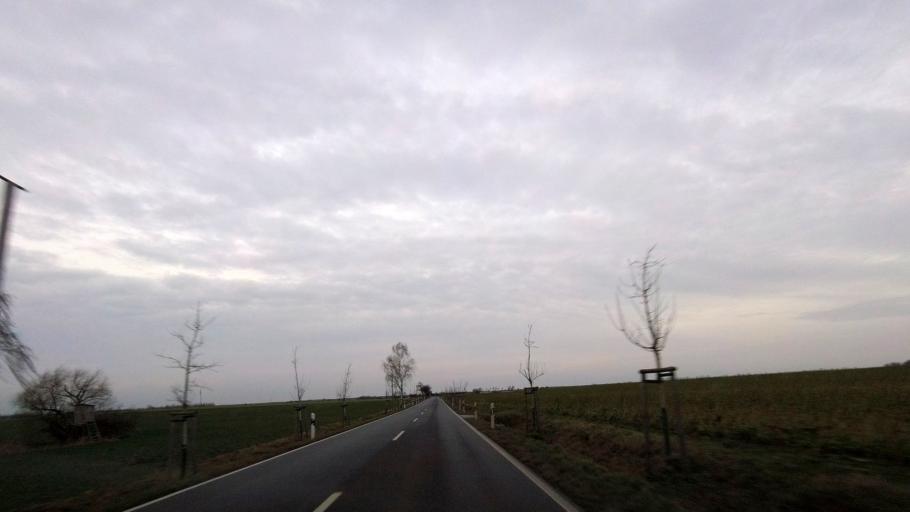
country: DE
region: Brandenburg
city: Niedergorsdorf
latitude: 51.9398
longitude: 12.9777
